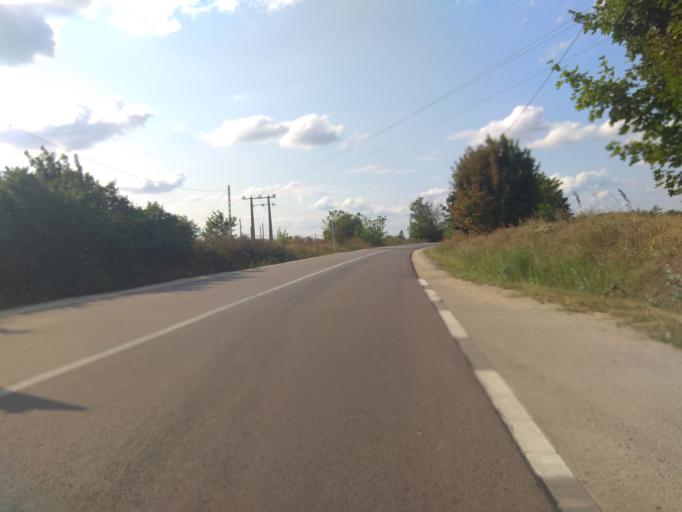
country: HU
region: Borsod-Abauj-Zemplen
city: Hejobaba
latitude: 47.8916
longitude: 20.8948
